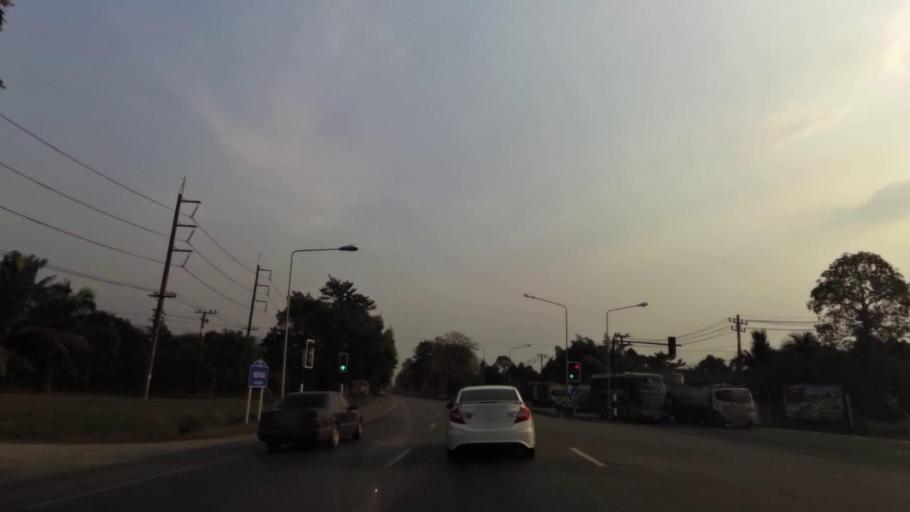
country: TH
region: Chanthaburi
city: Chanthaburi
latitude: 12.5300
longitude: 102.1577
